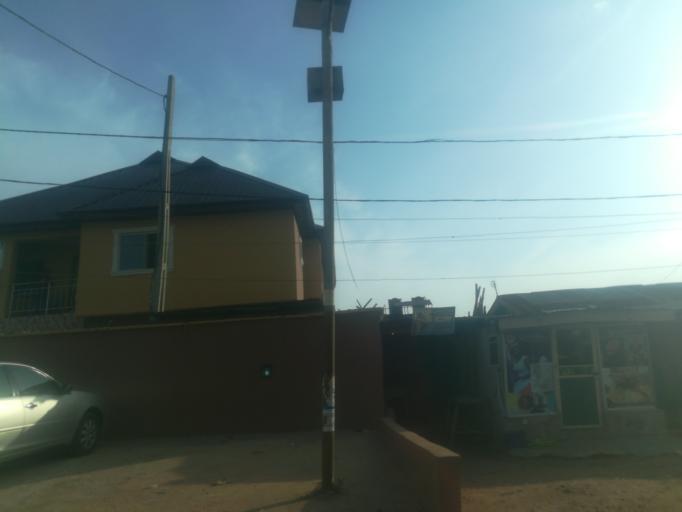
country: NG
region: Ogun
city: Abeokuta
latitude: 7.1186
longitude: 3.3208
